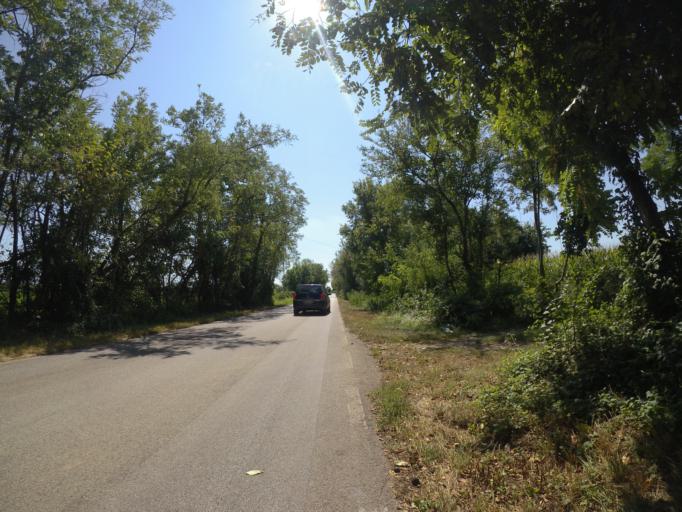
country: IT
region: Friuli Venezia Giulia
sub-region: Provincia di Udine
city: Mortegliano
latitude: 45.9611
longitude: 13.1658
